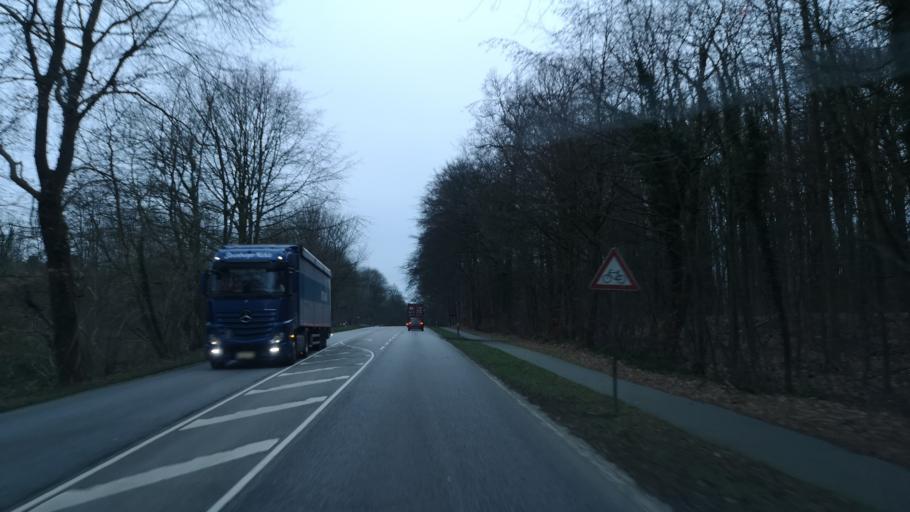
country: DE
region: Schleswig-Holstein
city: Itzehoe
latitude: 53.9379
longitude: 9.5383
